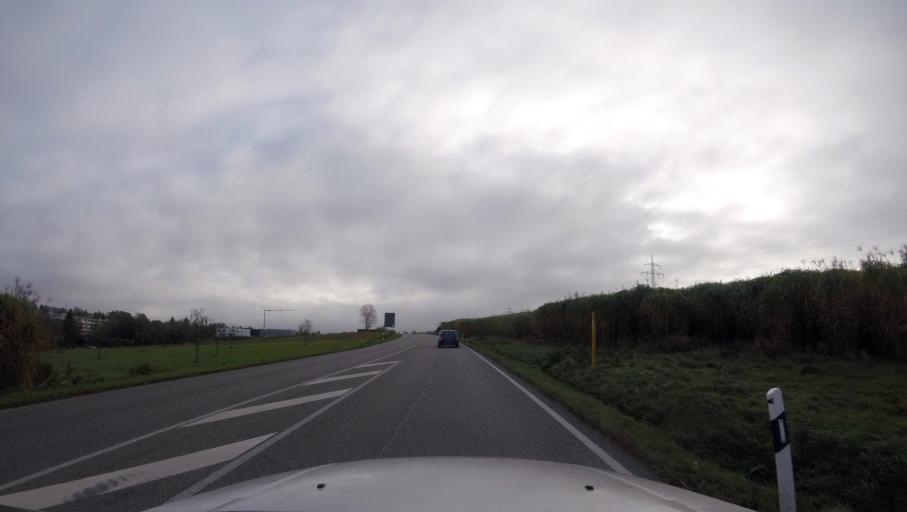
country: DE
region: Baden-Wuerttemberg
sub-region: Regierungsbezirk Stuttgart
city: Backnang
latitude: 48.9377
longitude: 9.4211
